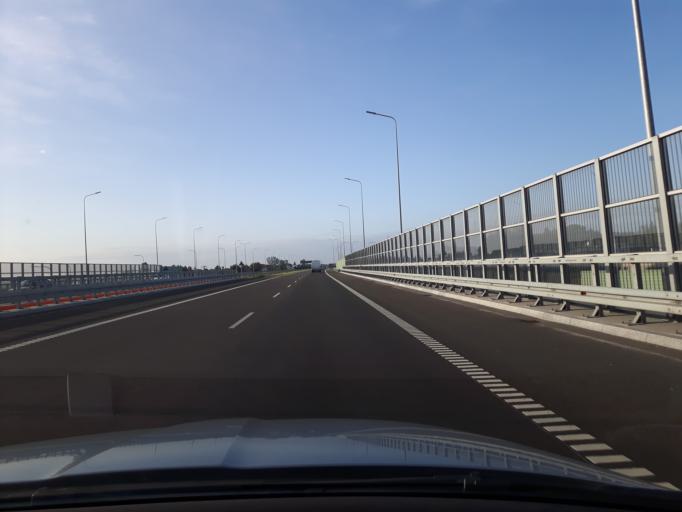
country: PL
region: Masovian Voivodeship
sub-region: Powiat radomski
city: Wolanow
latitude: 51.3894
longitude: 21.0210
